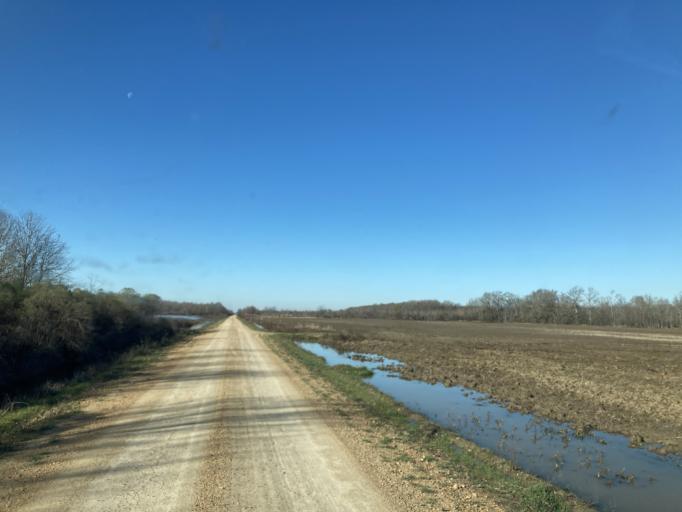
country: US
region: Mississippi
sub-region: Yazoo County
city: Yazoo City
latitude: 32.9518
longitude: -90.6178
